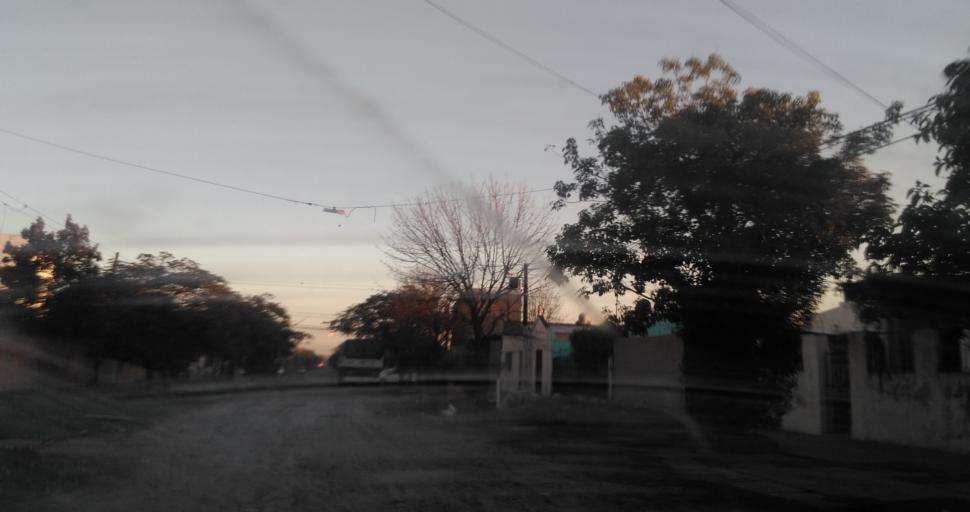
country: AR
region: Chaco
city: Resistencia
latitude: -27.4724
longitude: -58.9948
